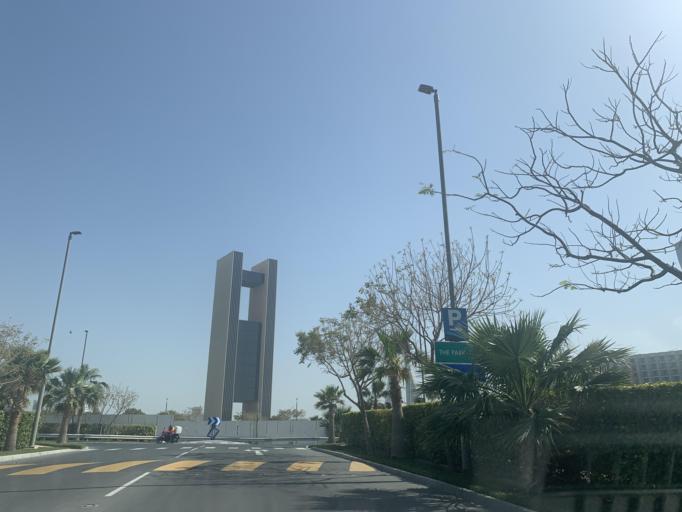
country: BH
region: Muharraq
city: Al Muharraq
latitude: 26.2517
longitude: 50.5792
